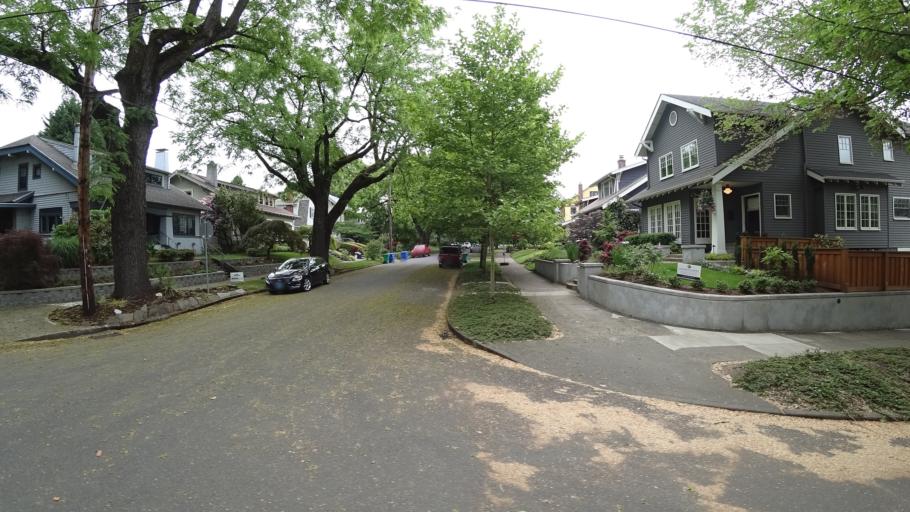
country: US
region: Oregon
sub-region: Multnomah County
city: Portland
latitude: 45.5256
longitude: -122.6188
